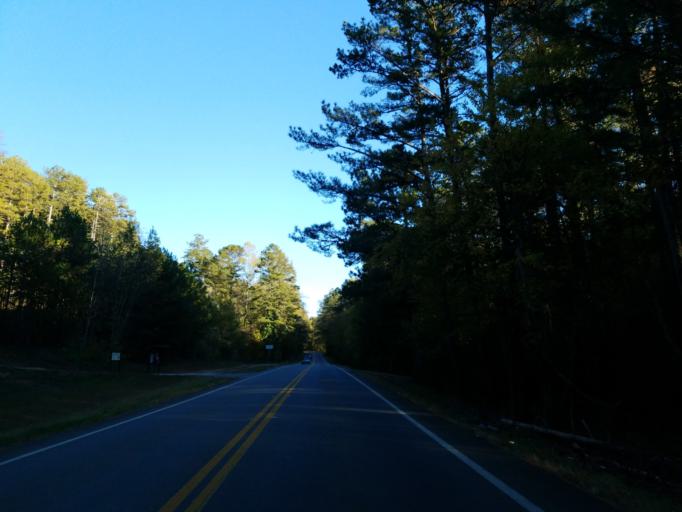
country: US
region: Georgia
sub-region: Dawson County
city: Dawsonville
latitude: 34.4234
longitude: -84.2069
